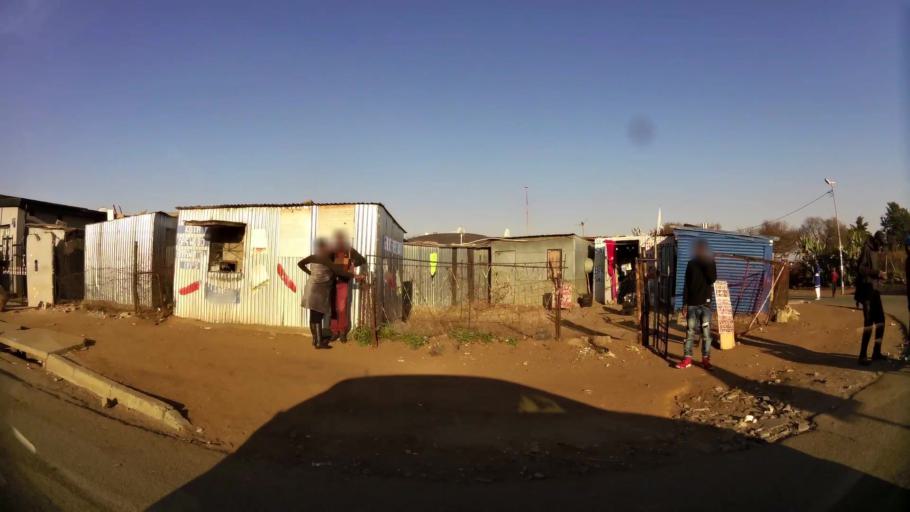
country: ZA
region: Gauteng
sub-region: City of Johannesburg Metropolitan Municipality
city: Soweto
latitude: -26.2566
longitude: 27.8792
